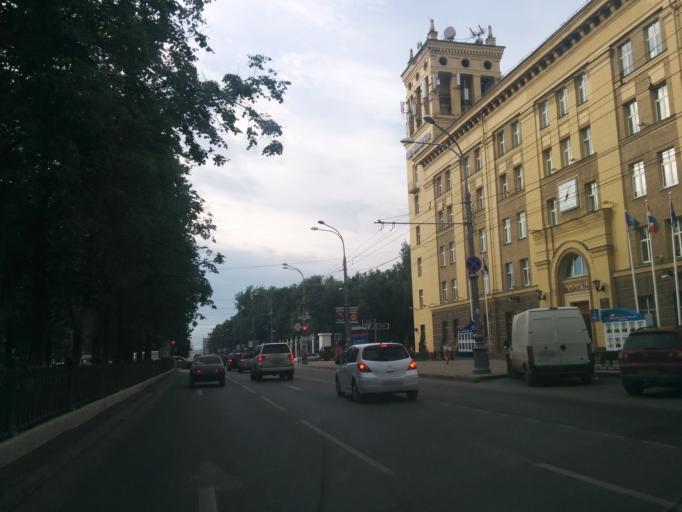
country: RU
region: Perm
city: Perm
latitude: 58.0018
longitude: 56.2481
